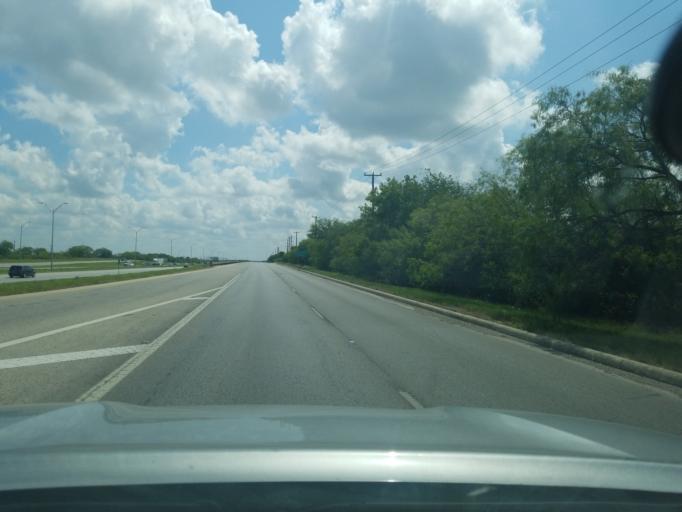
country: US
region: Texas
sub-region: Bexar County
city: San Antonio
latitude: 29.3197
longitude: -98.5285
